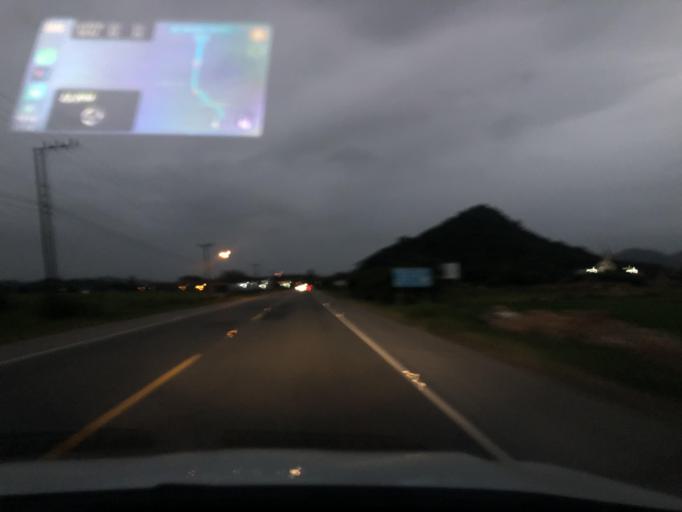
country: BR
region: Santa Catarina
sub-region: Jaragua Do Sul
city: Jaragua do Sul
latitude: -26.6082
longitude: -49.0086
